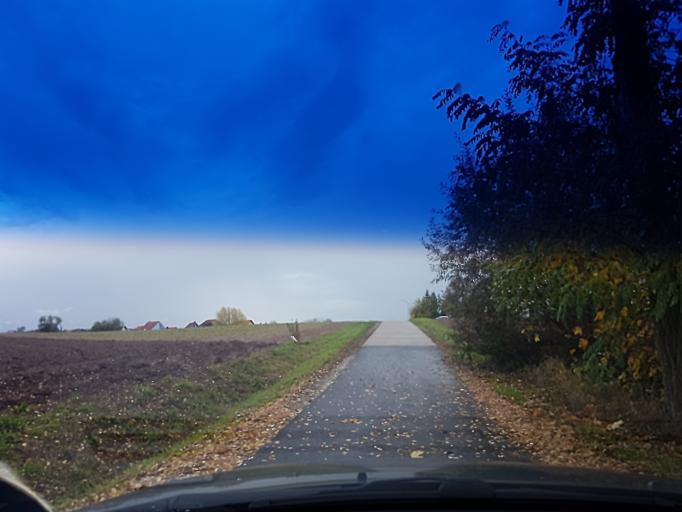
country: DE
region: Bavaria
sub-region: Upper Franconia
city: Schlusselfeld
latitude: 49.7577
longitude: 10.6292
